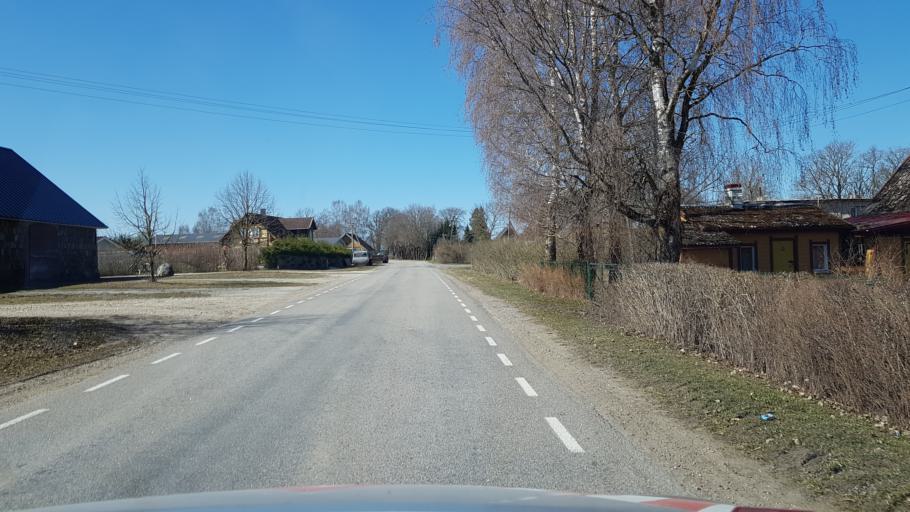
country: EE
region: Laeaene-Virumaa
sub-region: Vaeike-Maarja vald
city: Vaike-Maarja
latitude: 59.1120
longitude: 26.3730
